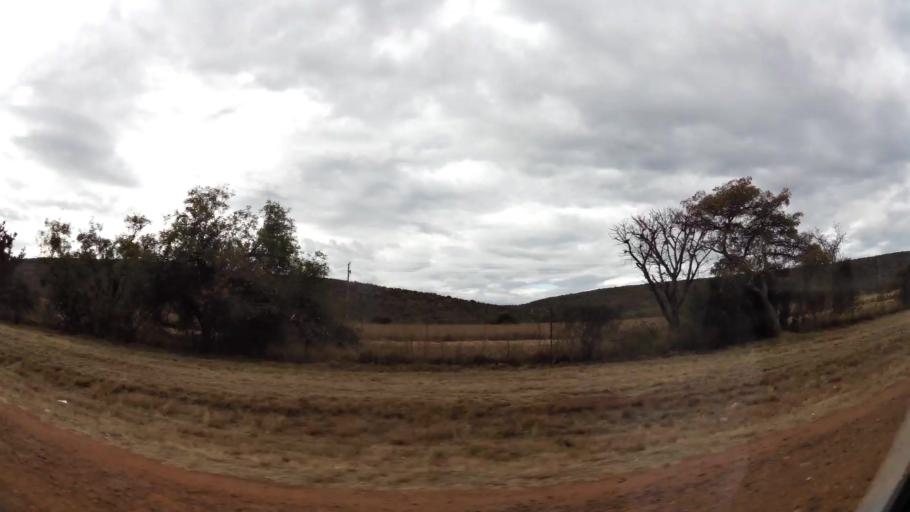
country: ZA
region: Limpopo
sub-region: Waterberg District Municipality
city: Modimolle
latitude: -24.6771
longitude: 28.5207
